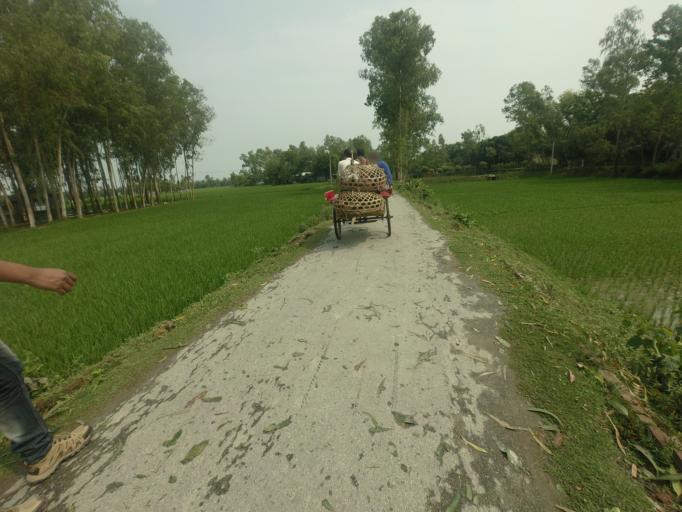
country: BD
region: Rajshahi
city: Sirajganj
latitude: 24.3220
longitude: 89.6818
